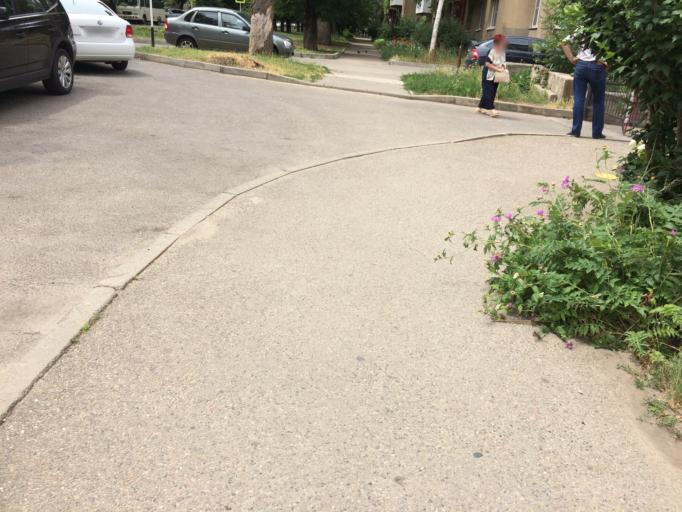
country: RU
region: Stavropol'skiy
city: Stavropol'
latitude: 45.0407
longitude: 41.9556
